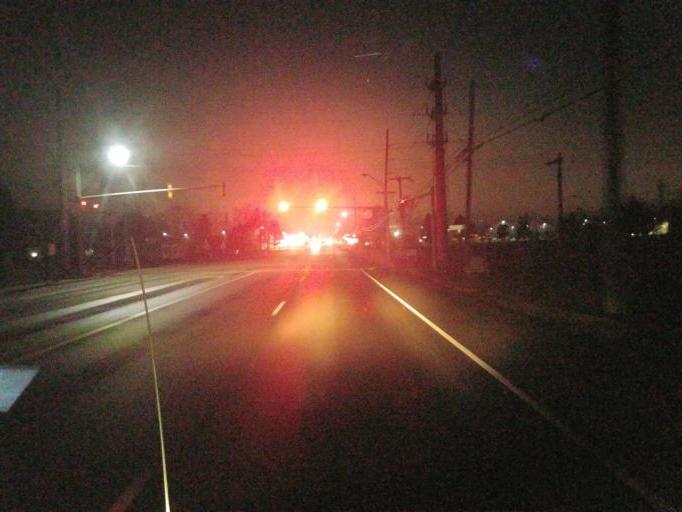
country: US
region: Ohio
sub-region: Williams County
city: Bryan
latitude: 41.4559
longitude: -84.5507
